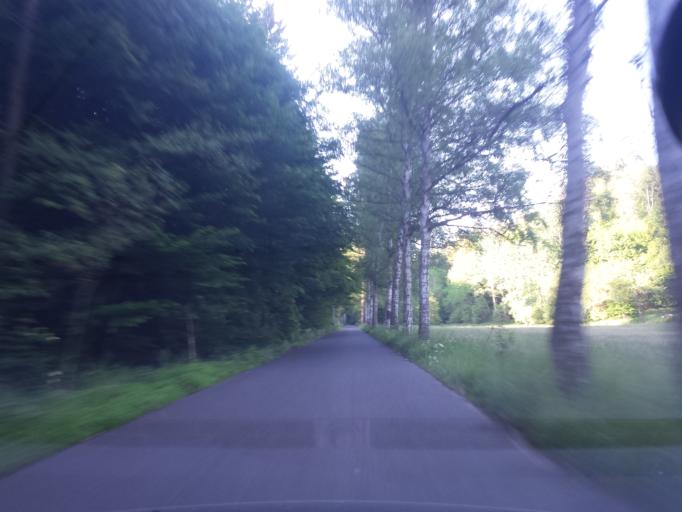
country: CZ
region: Central Bohemia
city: Mseno
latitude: 50.4524
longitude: 14.5850
